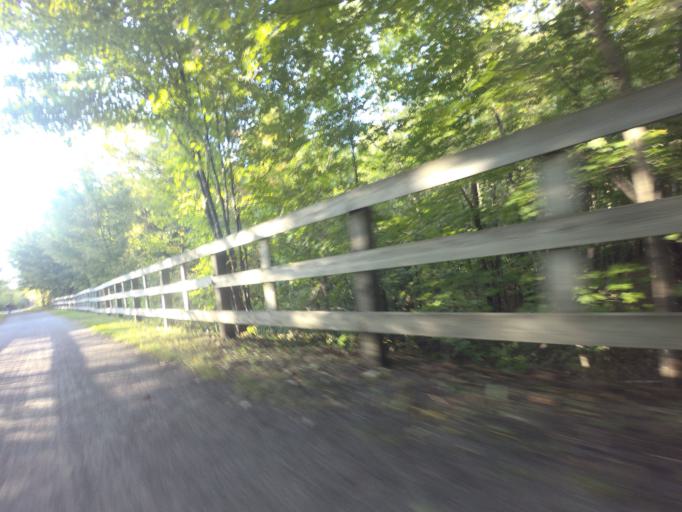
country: CA
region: Quebec
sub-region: Laurentides
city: Saint-Jerome
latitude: 45.8152
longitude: -74.0441
